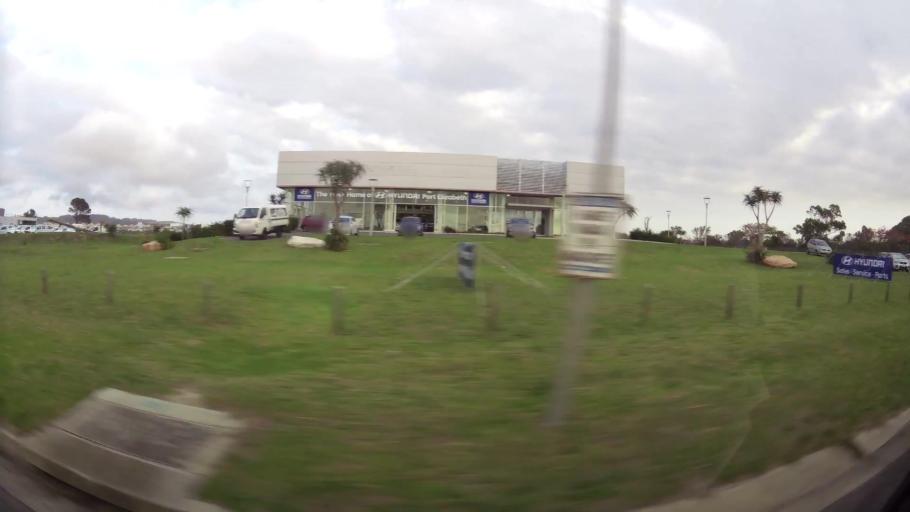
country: ZA
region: Eastern Cape
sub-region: Nelson Mandela Bay Metropolitan Municipality
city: Port Elizabeth
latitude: -33.9669
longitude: 25.5550
